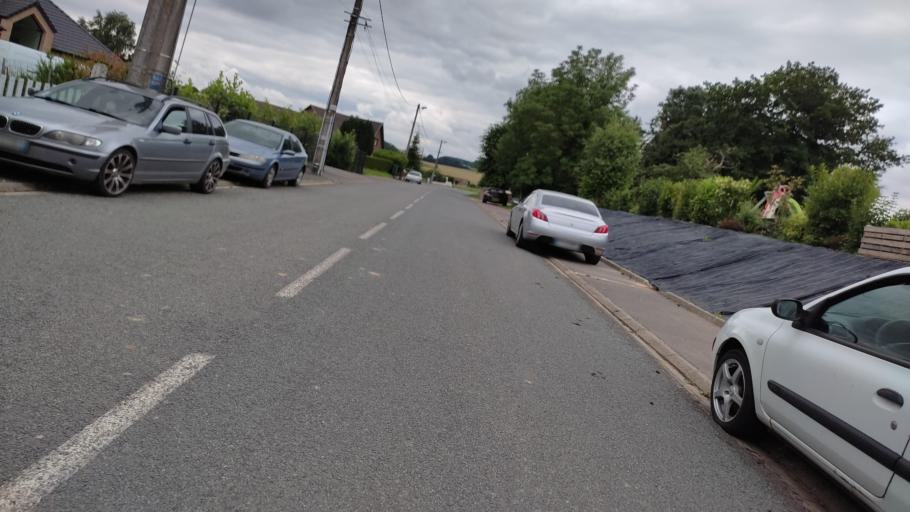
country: FR
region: Nord-Pas-de-Calais
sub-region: Departement du Pas-de-Calais
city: Beaumetz-les-Loges
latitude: 50.2542
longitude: 2.6426
